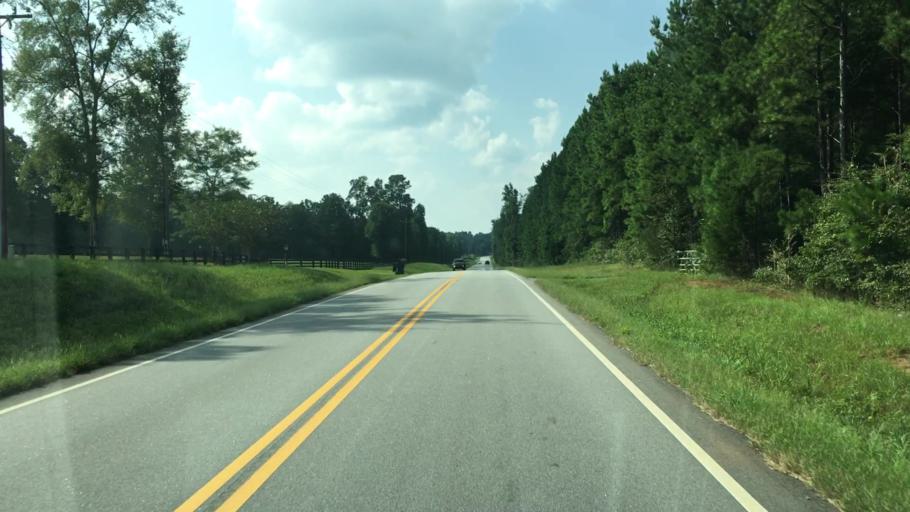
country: US
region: Georgia
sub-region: Jasper County
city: Monticello
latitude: 33.3901
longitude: -83.7527
